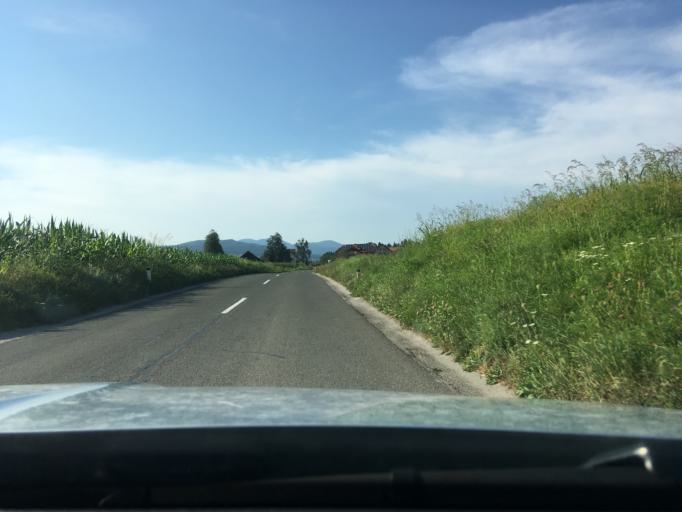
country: SI
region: Crnomelj
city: Crnomelj
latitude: 45.5389
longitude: 15.1612
